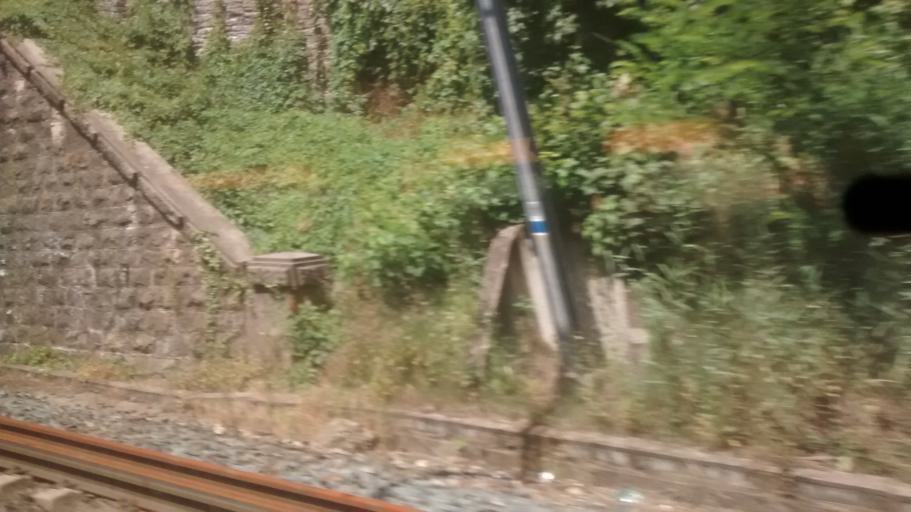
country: FR
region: Rhone-Alpes
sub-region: Departement du Rhone
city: Caluire-et-Cuire
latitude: 45.7925
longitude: 4.8682
